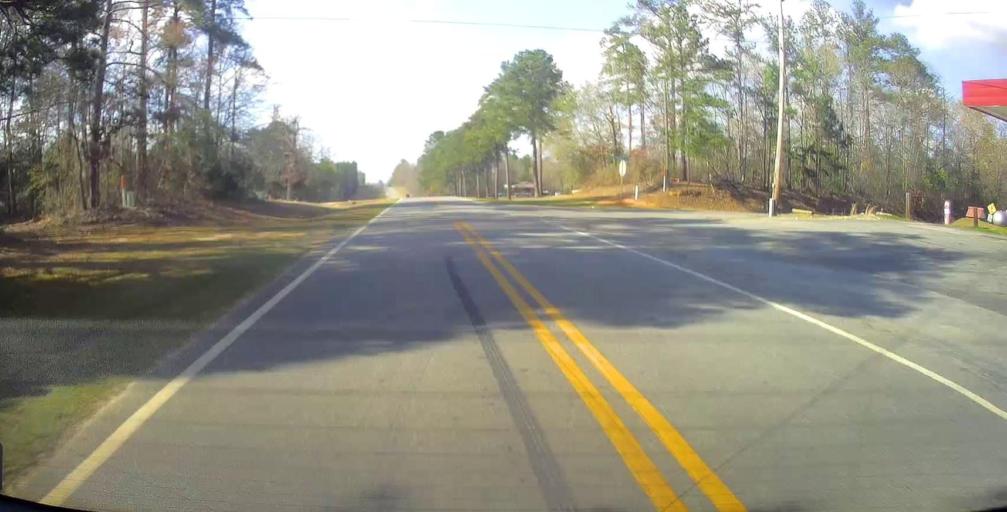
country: US
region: Georgia
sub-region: Laurens County
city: Dublin
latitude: 32.6179
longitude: -83.0861
